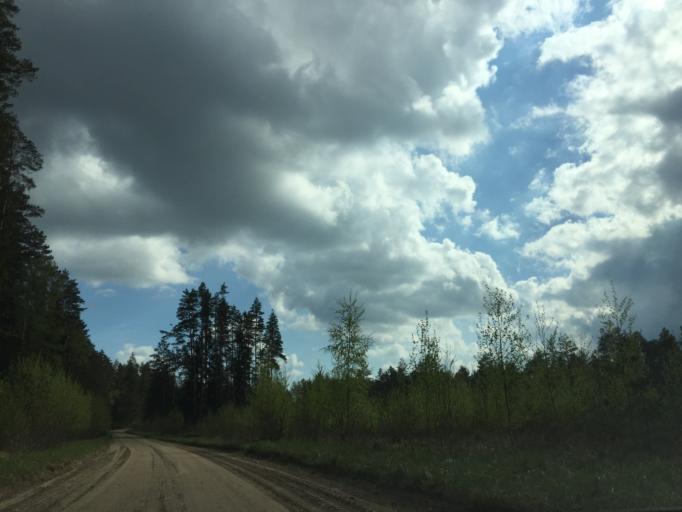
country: LV
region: Sigulda
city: Sigulda
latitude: 57.2998
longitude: 24.8836
